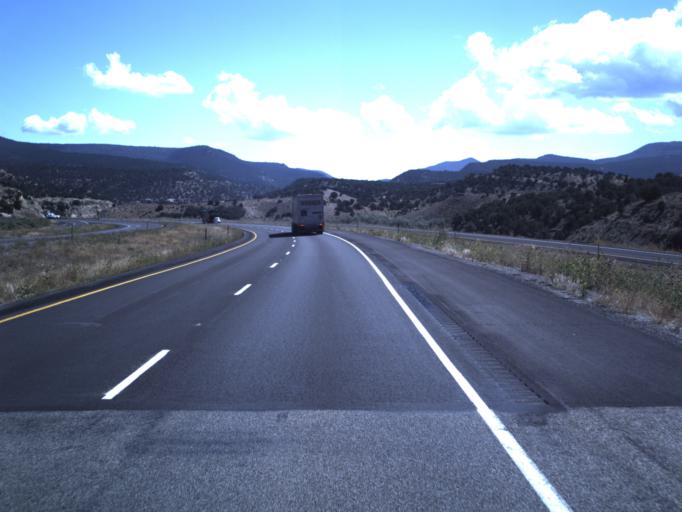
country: US
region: Utah
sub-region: Sevier County
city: Salina
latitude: 38.9159
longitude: -111.7380
